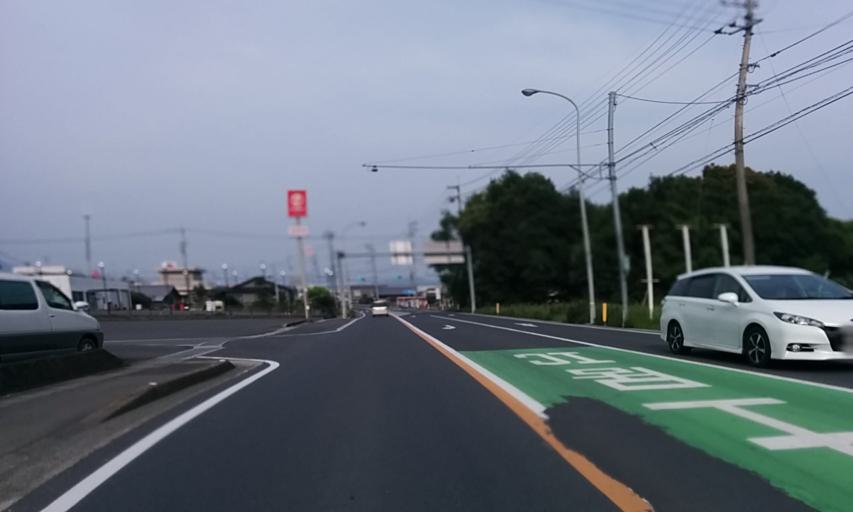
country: JP
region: Ehime
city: Kawanoecho
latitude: 33.9650
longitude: 133.4680
